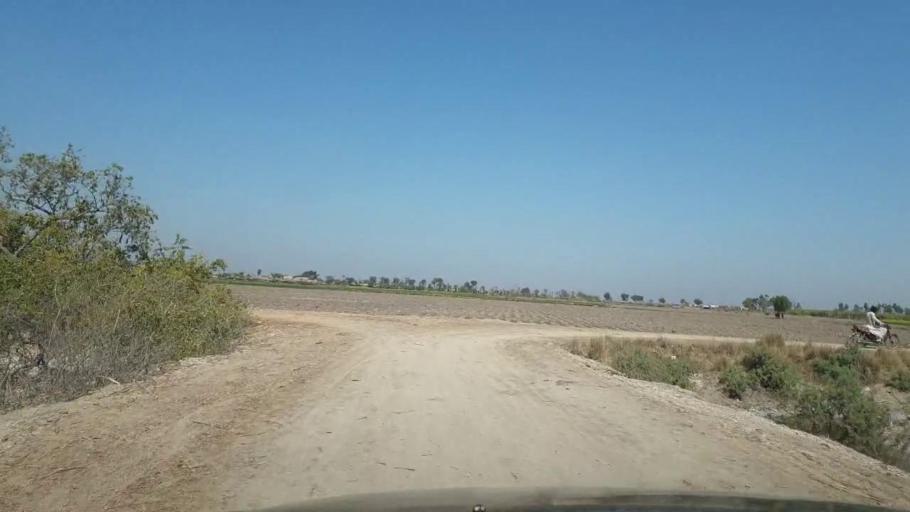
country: PK
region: Sindh
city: Mirpur Khas
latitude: 25.5663
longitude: 69.0828
